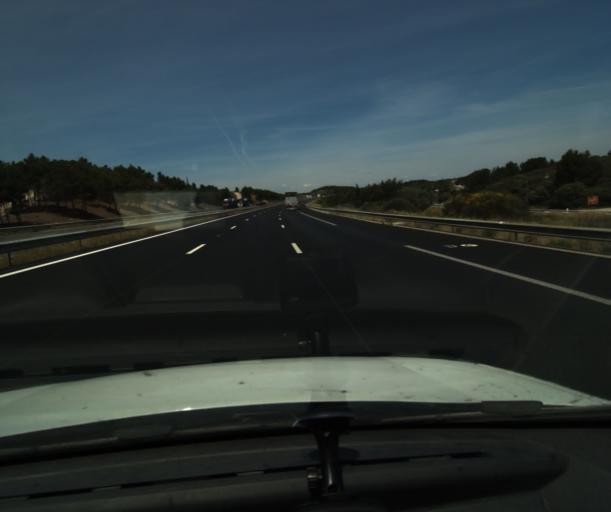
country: FR
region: Languedoc-Roussillon
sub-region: Departement de l'Aude
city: Portel-des-Corbieres
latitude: 43.0638
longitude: 2.9369
